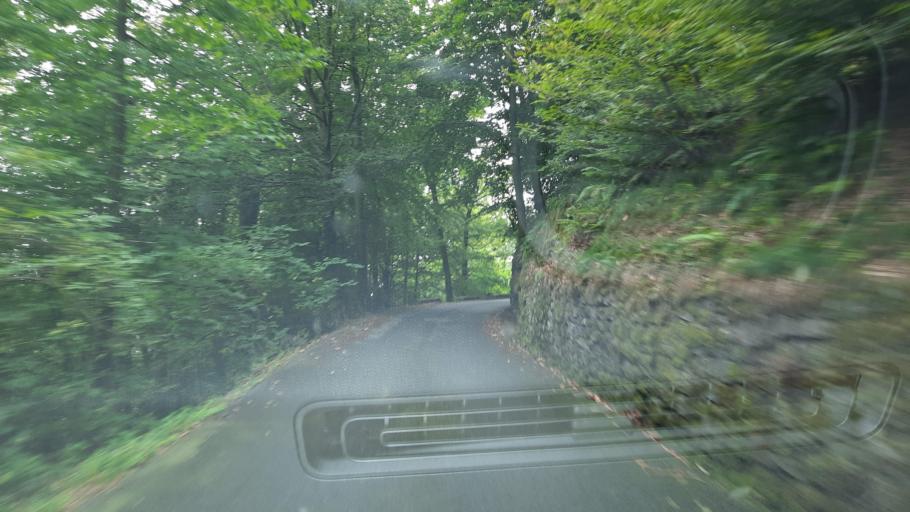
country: IT
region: Piedmont
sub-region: Provincia di Biella
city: San Paolo Cervo
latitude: 45.6557
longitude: 8.0029
